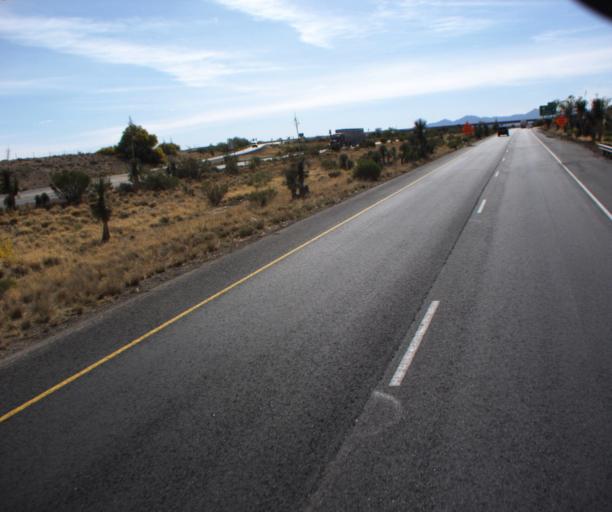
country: US
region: Arizona
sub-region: Pima County
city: Vail
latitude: 32.0103
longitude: -110.6956
